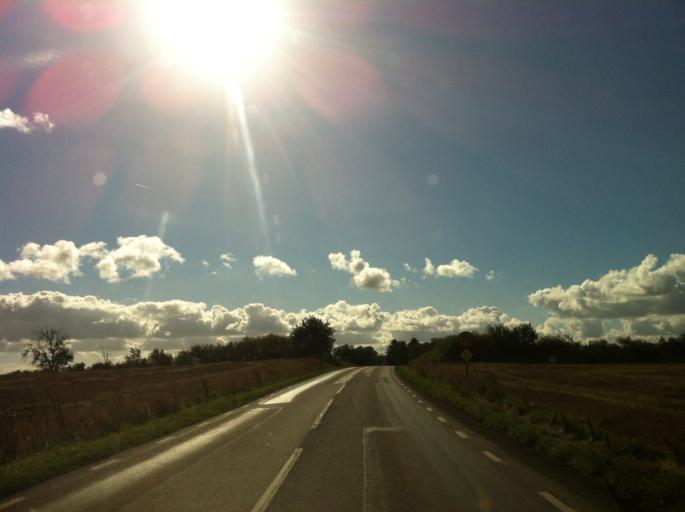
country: SE
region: Skane
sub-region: Sjobo Kommun
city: Sjoebo
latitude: 55.6522
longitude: 13.8121
